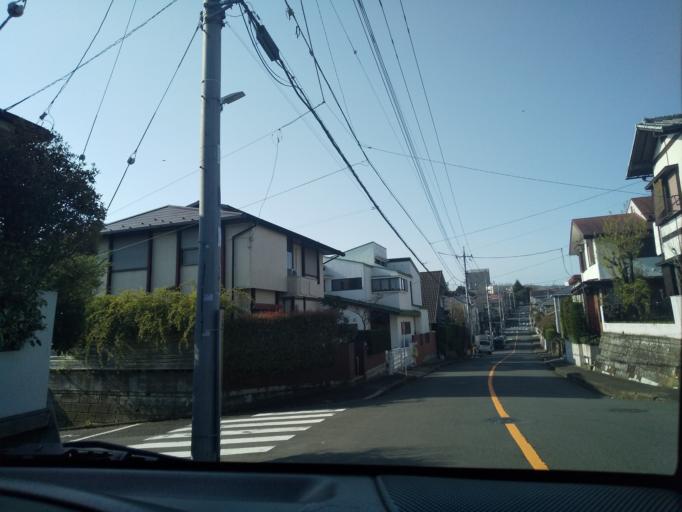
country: JP
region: Tokyo
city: Hino
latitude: 35.6512
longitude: 139.4247
